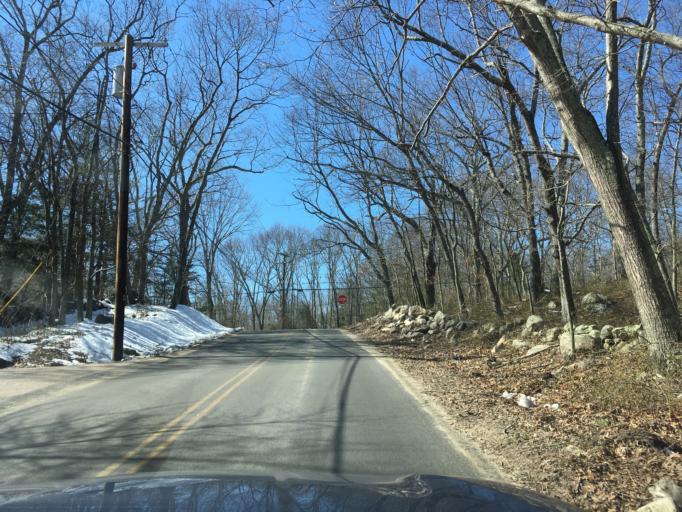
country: US
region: Rhode Island
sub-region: Washington County
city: Exeter
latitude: 41.6084
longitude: -71.5099
